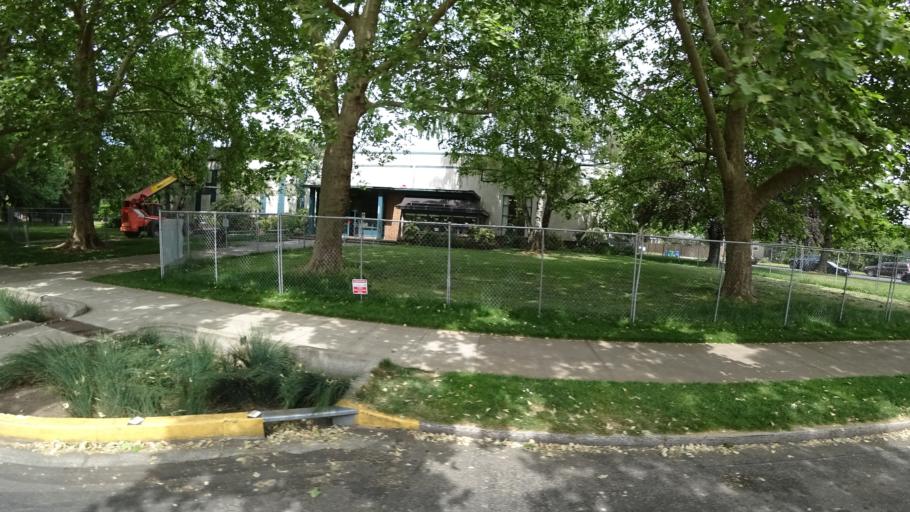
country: US
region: Oregon
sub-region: Washington County
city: West Haven
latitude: 45.5918
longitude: -122.7523
